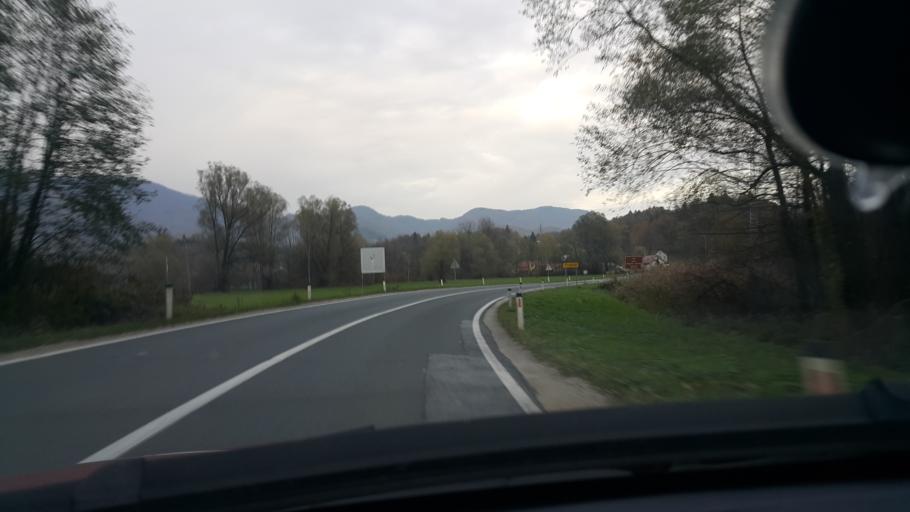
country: SI
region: Smarje pri Jelsah
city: Smarje pri Jelsah
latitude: 46.2436
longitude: 15.5698
